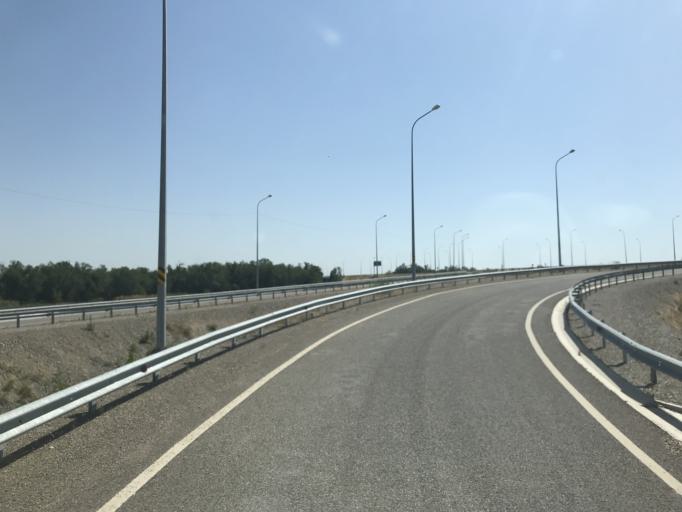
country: KZ
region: Zhambyl
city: Taraz
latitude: 42.9958
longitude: 71.2357
